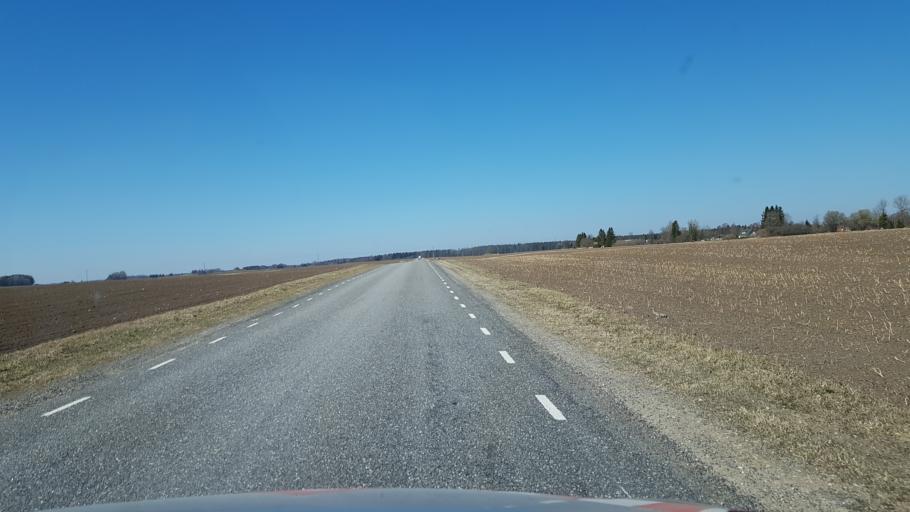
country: EE
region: Laeaene-Virumaa
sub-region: Rakke vald
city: Rakke
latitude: 59.0021
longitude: 26.1940
